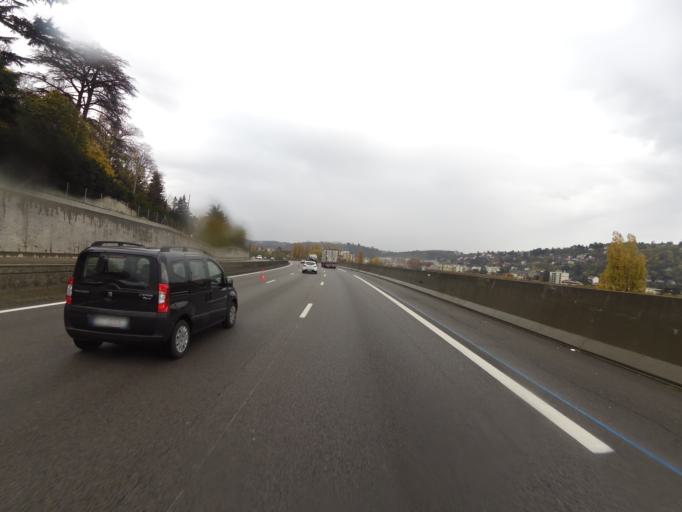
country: FR
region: Rhone-Alpes
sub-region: Departement du Rhone
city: Saint-Cyr-sur-le-Rhone
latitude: 45.5154
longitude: 4.8572
